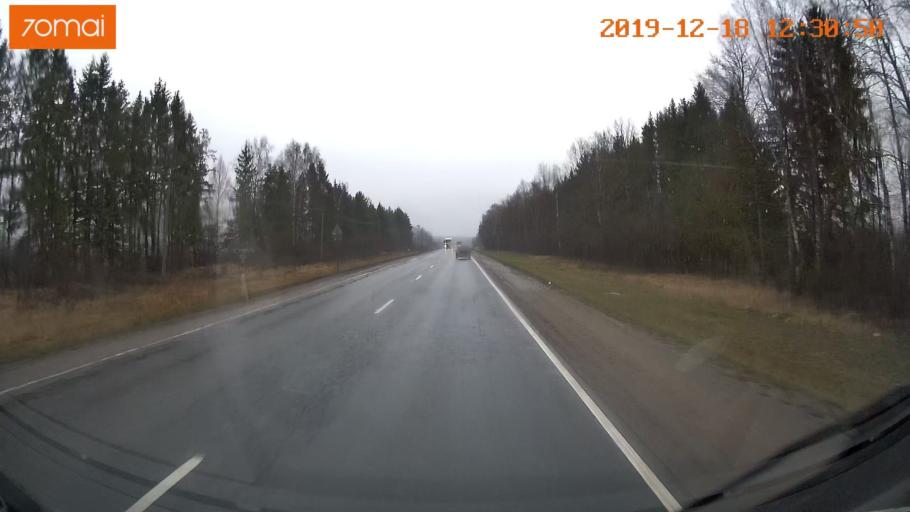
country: RU
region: Moskovskaya
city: Novopetrovskoye
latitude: 56.0941
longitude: 36.5371
